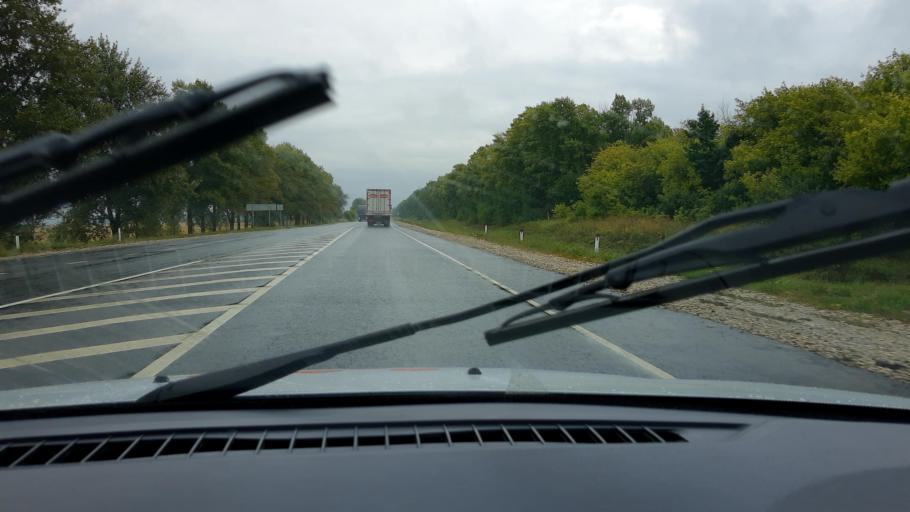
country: RU
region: Chuvashia
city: Yantikovo
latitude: 55.7897
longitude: 47.6980
